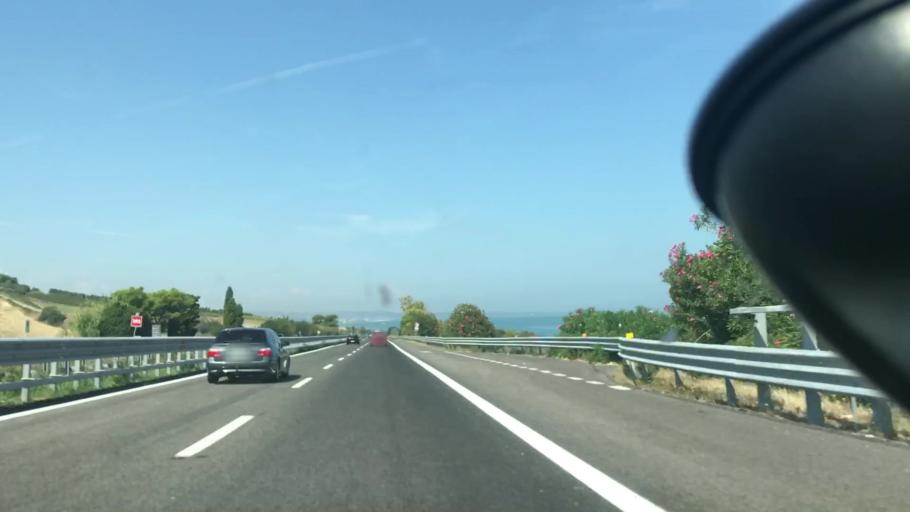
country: IT
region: Molise
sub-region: Provincia di Campobasso
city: Petacciato
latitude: 42.0219
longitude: 14.8885
